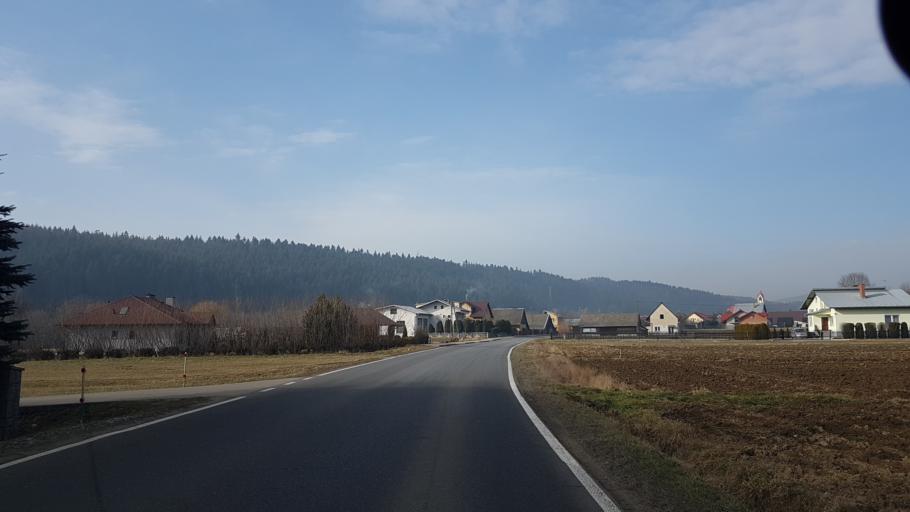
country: PL
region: Lesser Poland Voivodeship
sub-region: Powiat nowosadecki
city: Podegrodzie
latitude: 49.5611
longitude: 20.5600
